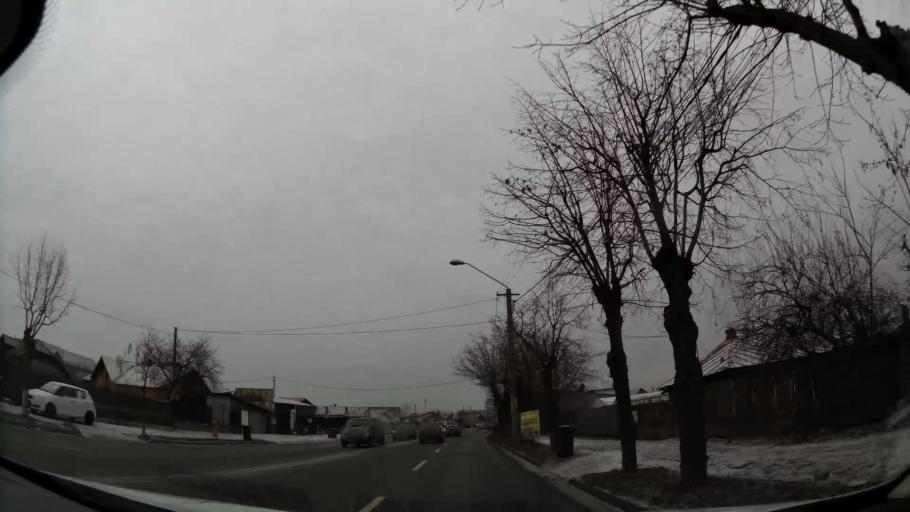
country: RO
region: Dambovita
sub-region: Comuna Ulmi
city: Ulmi
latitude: 44.9116
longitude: 25.4858
